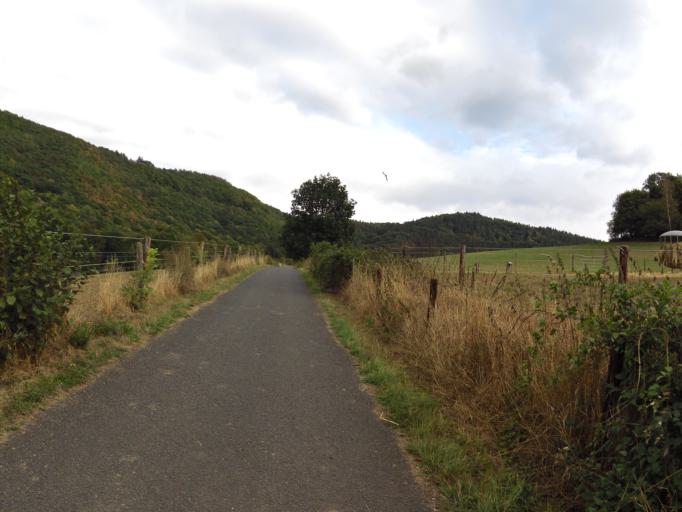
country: DE
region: North Rhine-Westphalia
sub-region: Regierungsbezirk Koln
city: Nideggen
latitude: 50.7005
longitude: 6.4570
